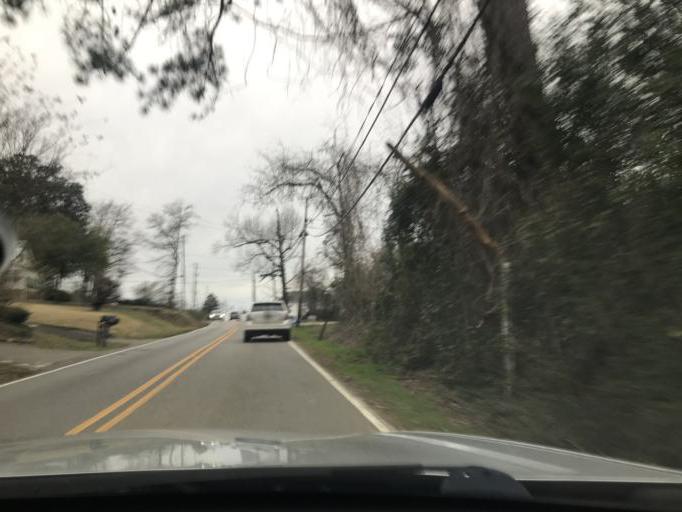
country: US
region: Alabama
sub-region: Jefferson County
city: Cahaba Heights
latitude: 33.4541
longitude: -86.7243
